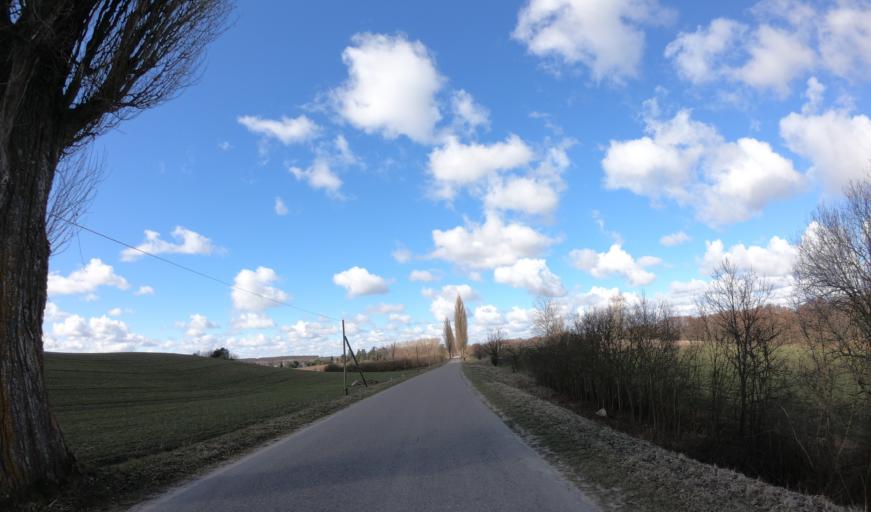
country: PL
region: West Pomeranian Voivodeship
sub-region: Powiat drawski
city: Drawsko Pomorskie
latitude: 53.4856
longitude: 15.8745
